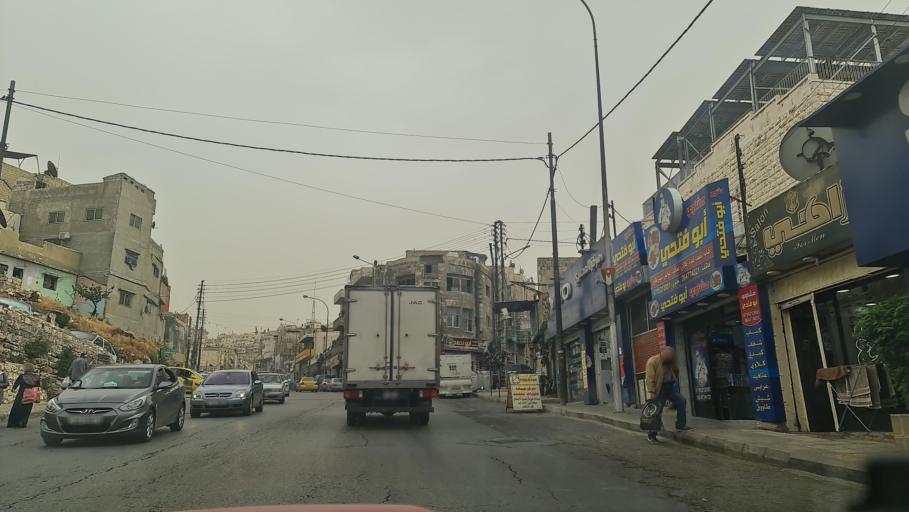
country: JO
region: Amman
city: Amman
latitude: 31.9435
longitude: 35.9291
